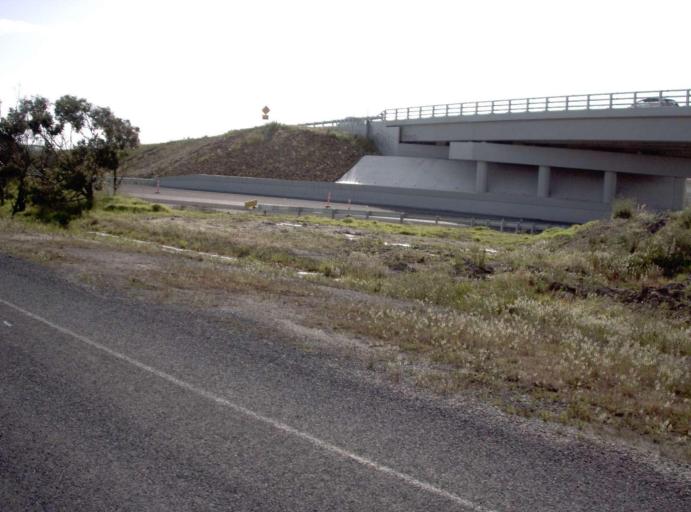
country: AU
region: Victoria
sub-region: Bass Coast
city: North Wonthaggi
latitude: -38.5076
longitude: 145.4515
